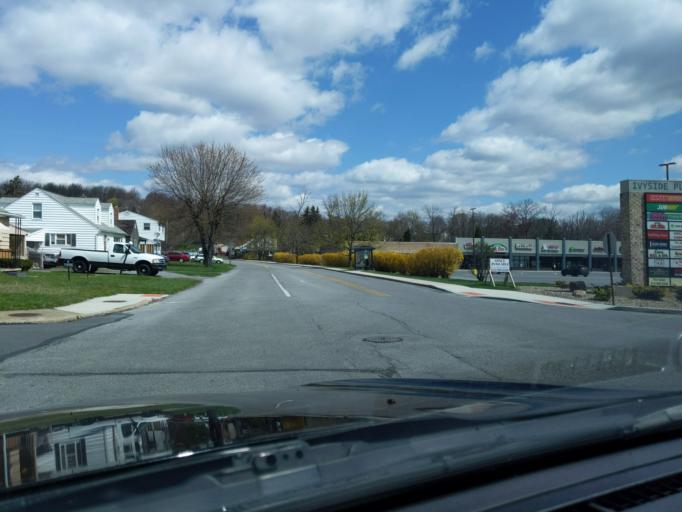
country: US
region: Pennsylvania
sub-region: Blair County
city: Altoona
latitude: 40.5361
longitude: -78.4009
